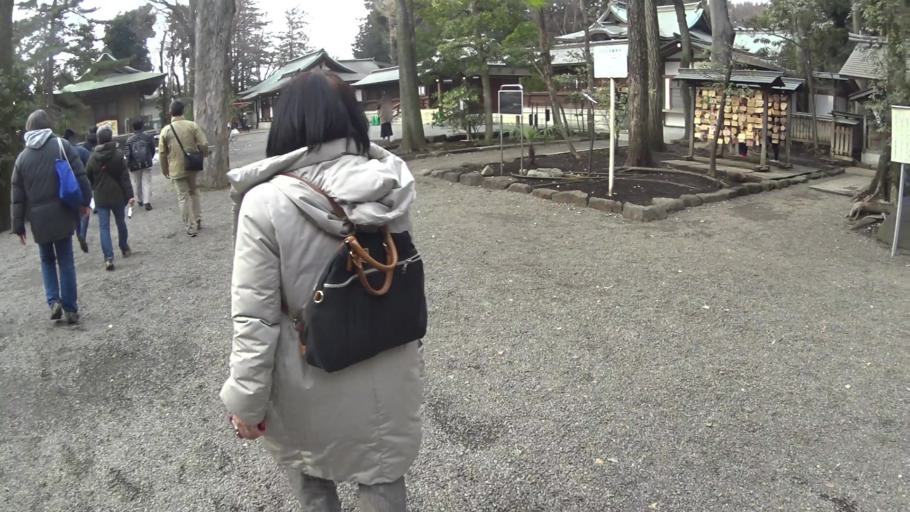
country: JP
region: Tokyo
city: Musashino
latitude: 35.7158
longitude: 139.5956
